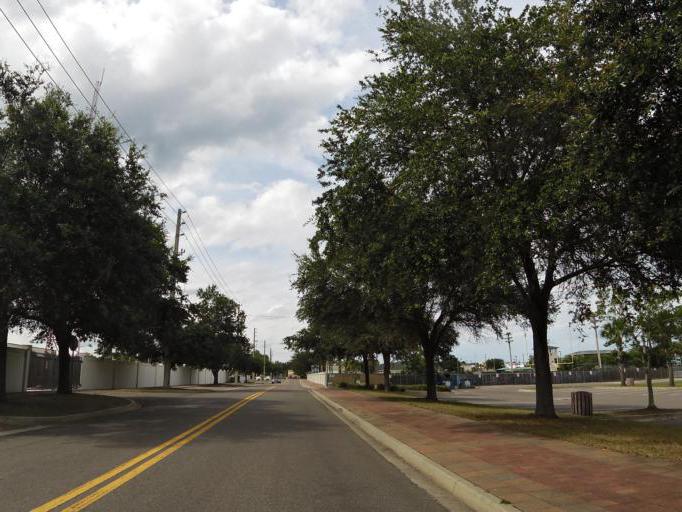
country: US
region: Florida
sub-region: Duval County
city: Jacksonville Beach
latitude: 30.2838
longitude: -81.4045
